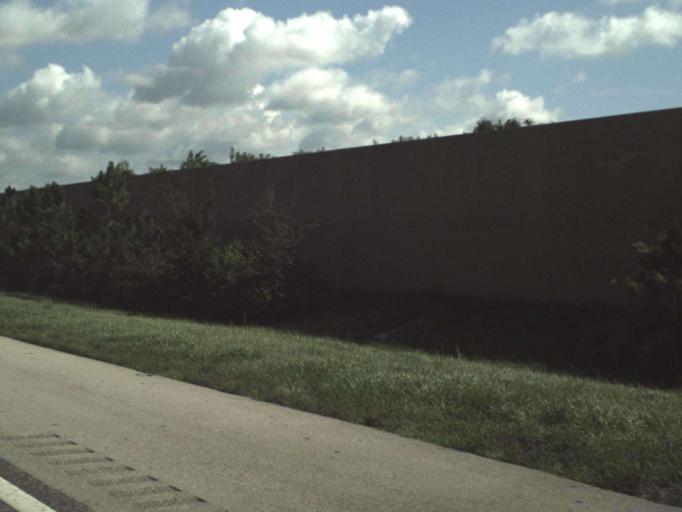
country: US
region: Florida
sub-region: Palm Beach County
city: Limestone Creek
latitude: 26.8930
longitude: -80.1339
